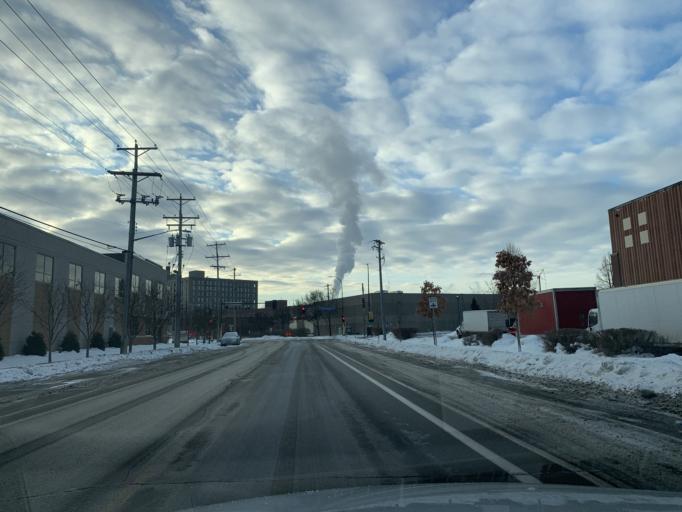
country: US
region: Minnesota
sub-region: Hennepin County
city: Minneapolis
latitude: 44.9929
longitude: -93.2799
